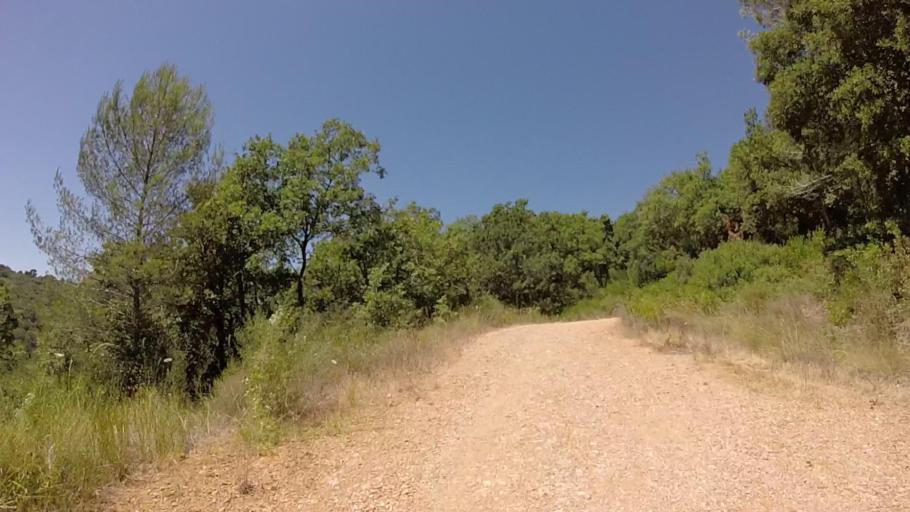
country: FR
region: Provence-Alpes-Cote d'Azur
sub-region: Departement des Alpes-Maritimes
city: Valbonne
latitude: 43.6320
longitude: 7.0328
